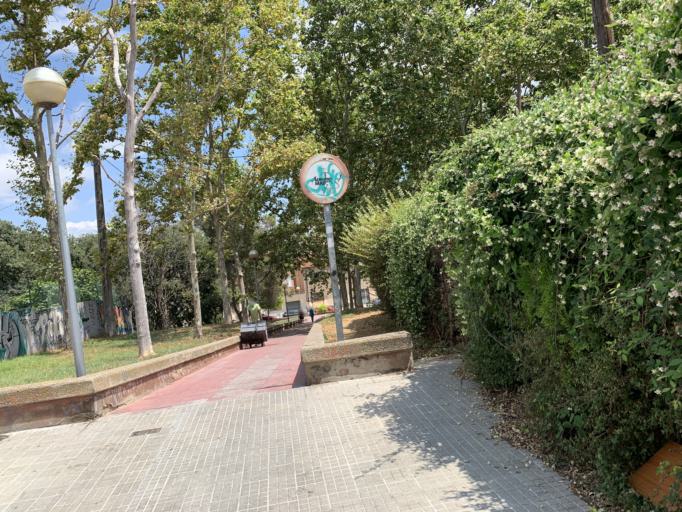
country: ES
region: Catalonia
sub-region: Provincia de Barcelona
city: Cerdanyola del Valles
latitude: 41.4943
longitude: 2.1386
